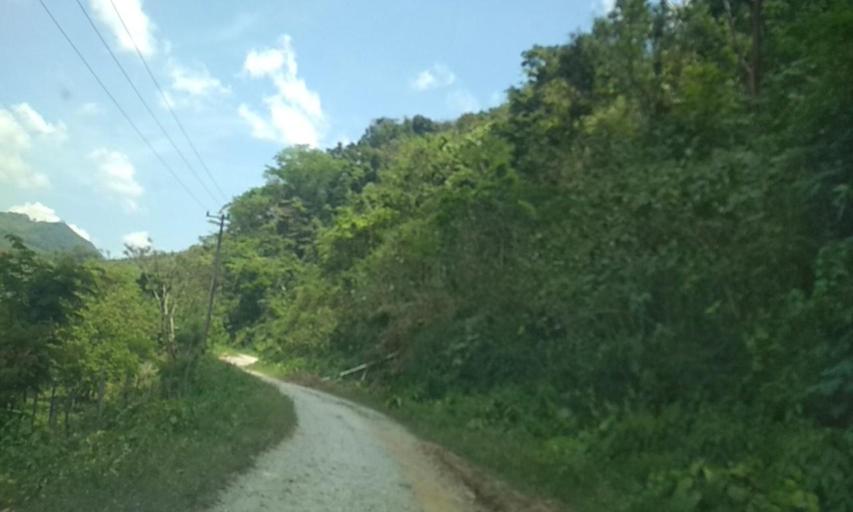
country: MX
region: Chiapas
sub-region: Tecpatan
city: Raudales Malpaso
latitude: 17.2927
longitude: -93.8414
